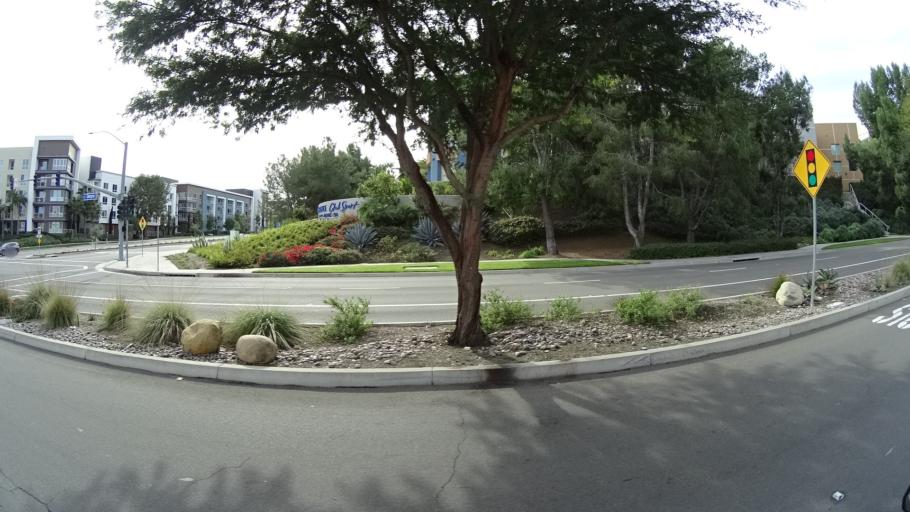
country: US
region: California
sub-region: Orange County
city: Aliso Viejo
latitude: 33.5831
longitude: -117.7292
